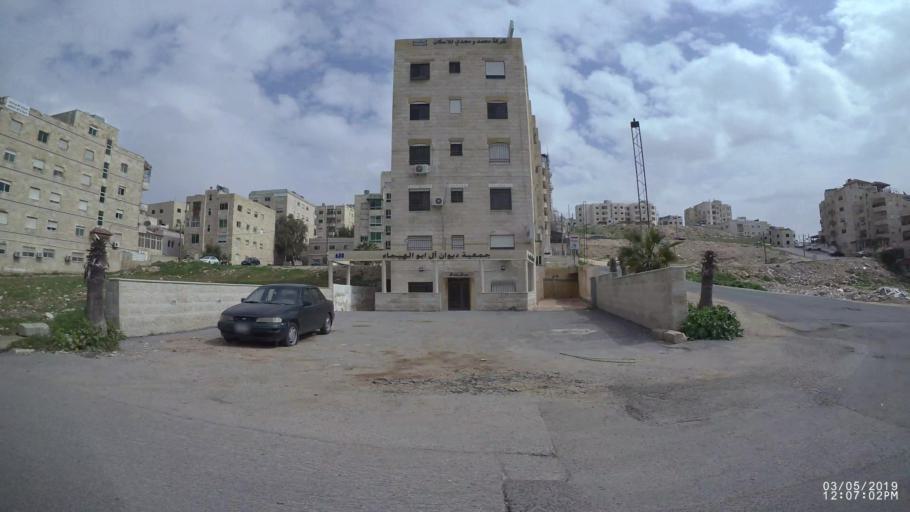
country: JO
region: Amman
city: Amman
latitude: 31.9906
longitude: 35.9180
